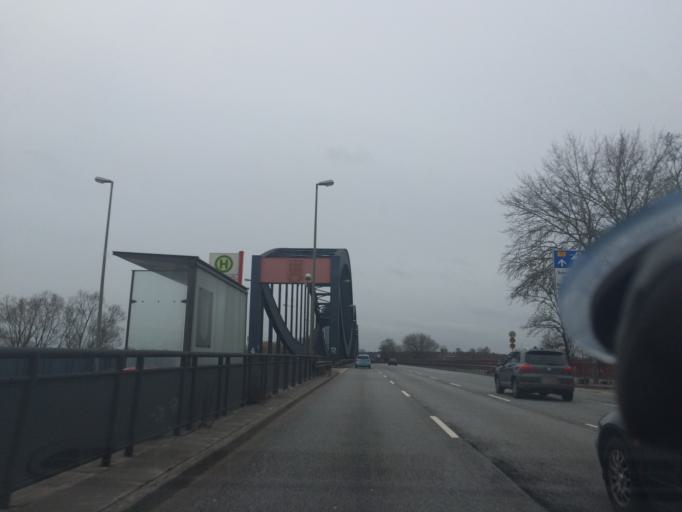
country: DE
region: Hamburg
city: Hammerbrook
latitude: 53.5338
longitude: 10.0278
